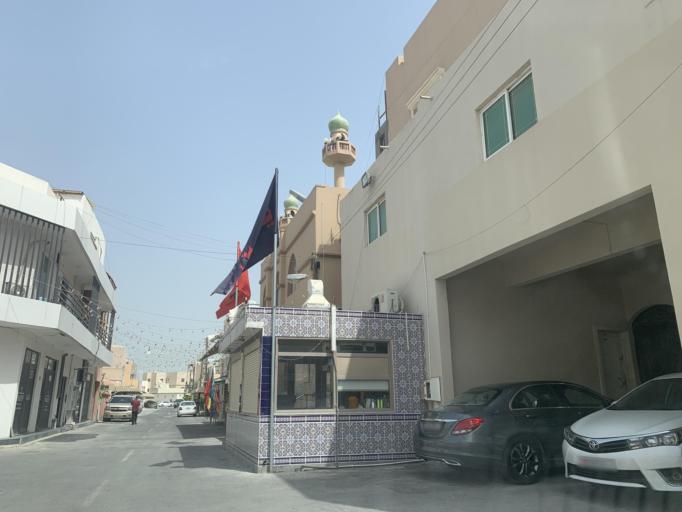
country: BH
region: Northern
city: Madinat `Isa
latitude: 26.1766
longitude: 50.5583
